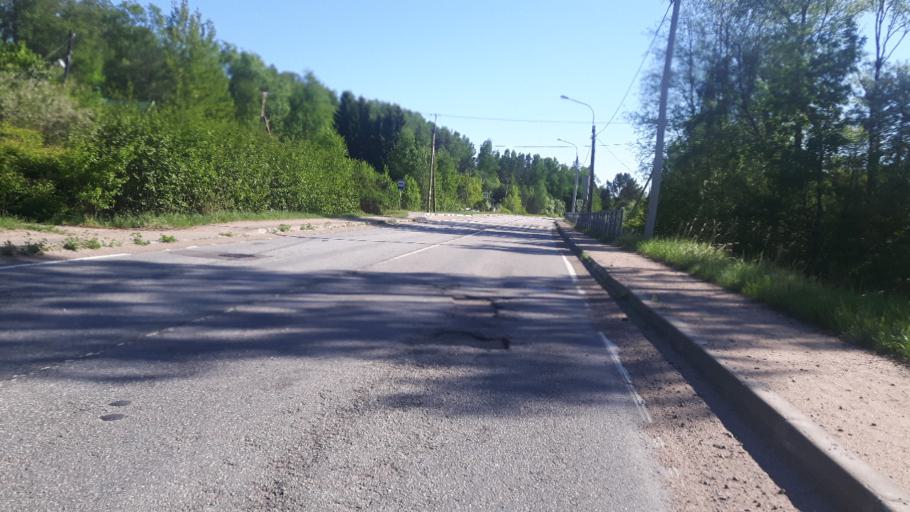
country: RU
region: Leningrad
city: Sosnovyy Bor
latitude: 60.2107
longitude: 29.0062
